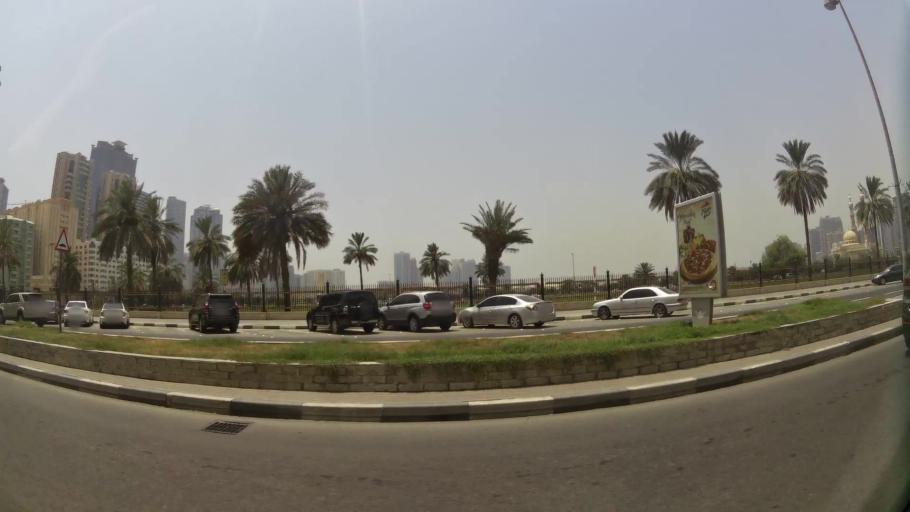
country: AE
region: Ash Shariqah
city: Sharjah
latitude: 25.3238
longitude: 55.3888
